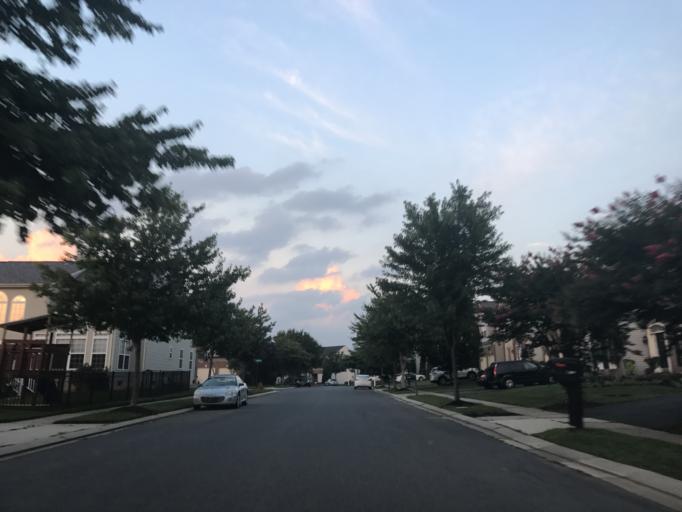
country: US
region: Maryland
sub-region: Baltimore County
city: White Marsh
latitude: 39.4053
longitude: -76.4311
